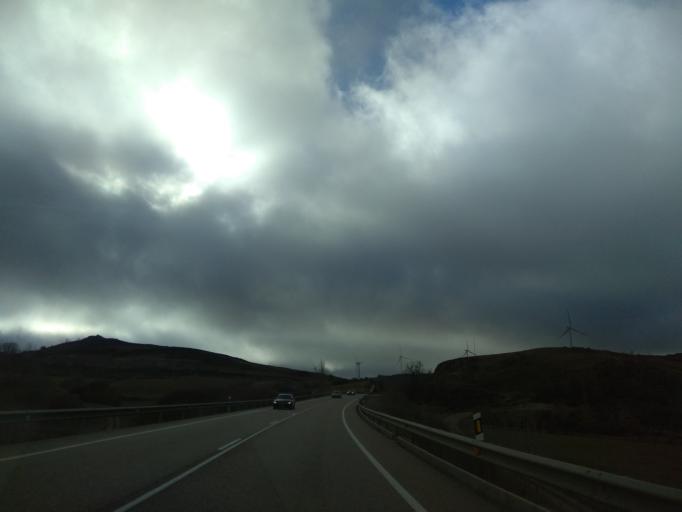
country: ES
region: Castille and Leon
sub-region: Provincia de Burgos
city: Montorio
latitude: 42.5910
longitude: -3.7853
